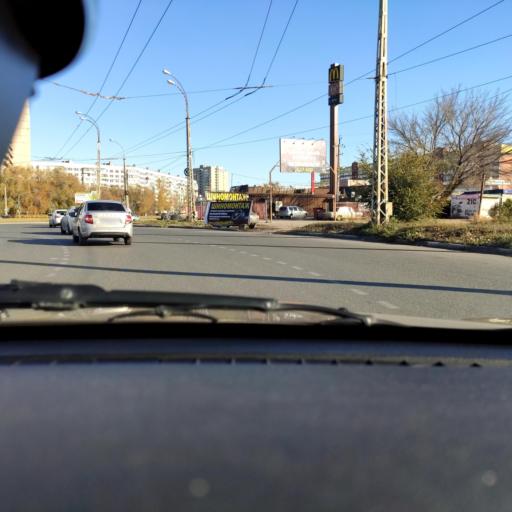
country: RU
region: Samara
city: Tol'yatti
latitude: 53.5170
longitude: 49.3109
